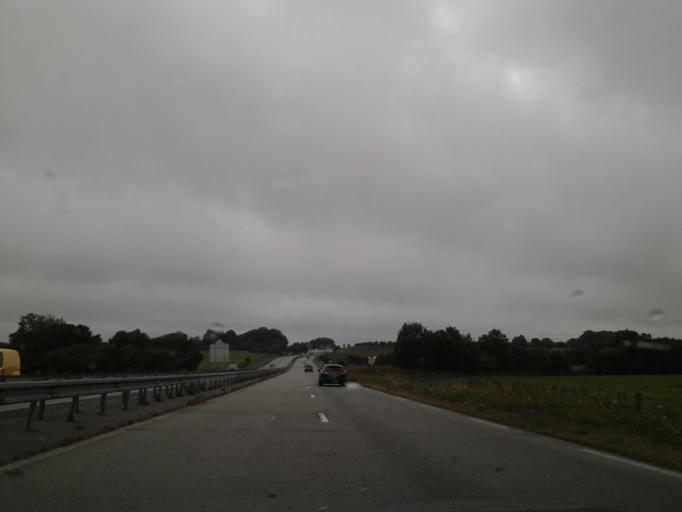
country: FR
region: Lower Normandy
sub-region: Departement de la Manche
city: Sainte-Mere-Eglise
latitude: 49.3899
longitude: -1.3032
